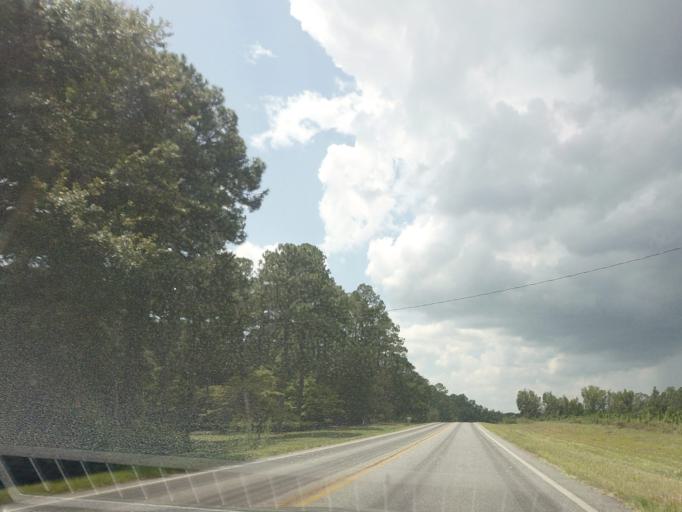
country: US
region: Georgia
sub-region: Bleckley County
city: Cochran
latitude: 32.3757
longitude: -83.3390
